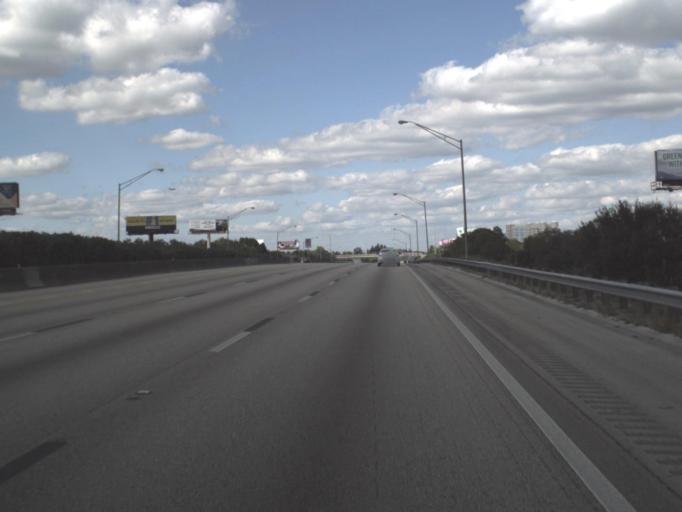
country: US
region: Florida
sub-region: Broward County
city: Davie
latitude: 26.0385
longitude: -80.2137
